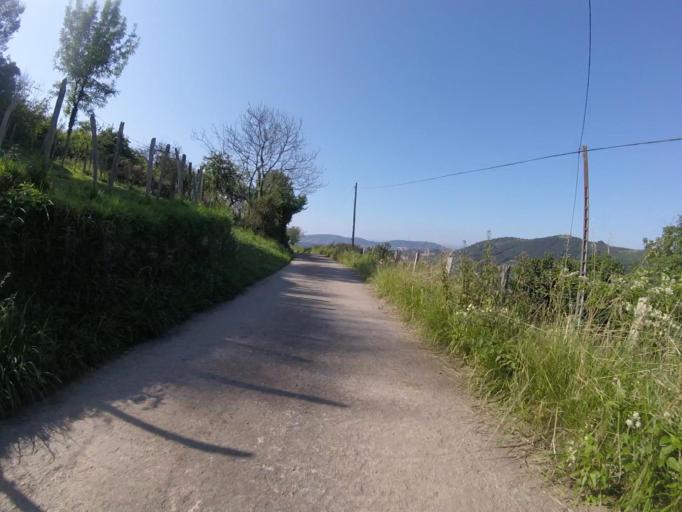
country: ES
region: Basque Country
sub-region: Provincia de Guipuzcoa
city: Astigarraga
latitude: 43.2764
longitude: -1.9303
